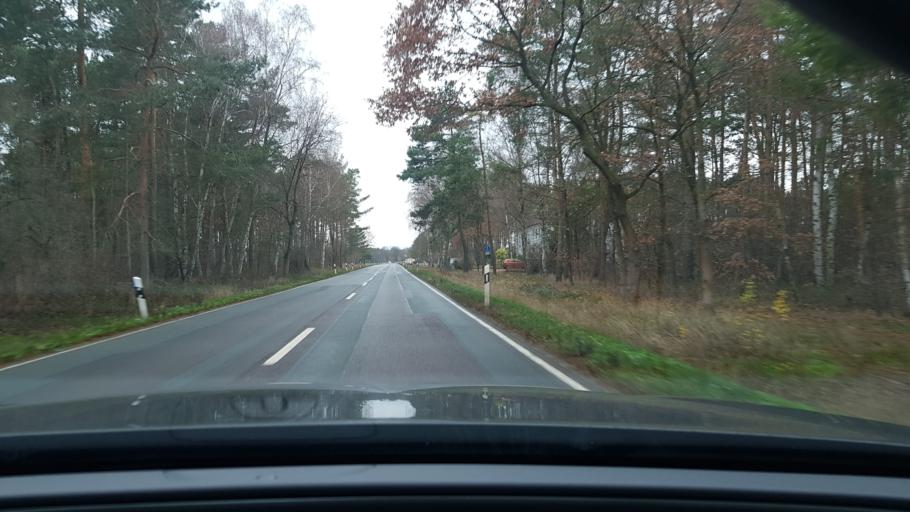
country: DE
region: Lower Saxony
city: Bahrdorf
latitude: 52.4159
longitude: 11.0605
